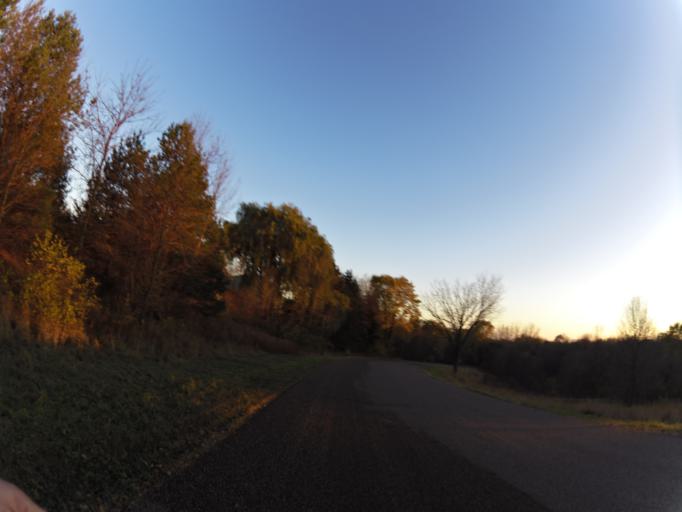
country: US
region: Minnesota
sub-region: Olmsted County
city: Rochester
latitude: 44.0466
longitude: -92.4080
